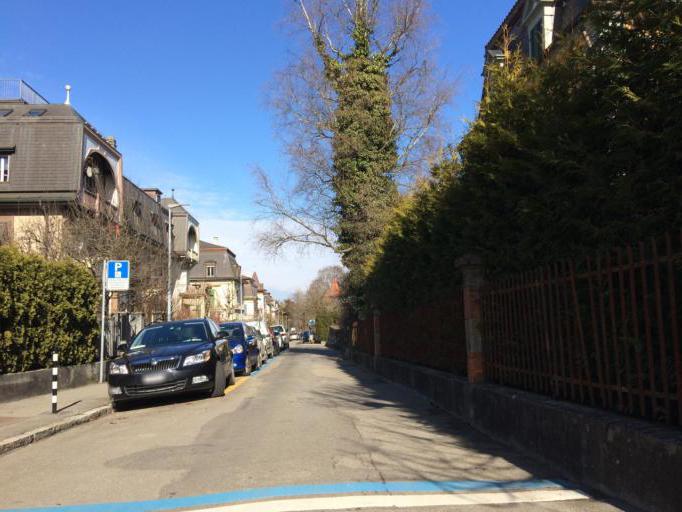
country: CH
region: Bern
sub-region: Bern-Mittelland District
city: Koniz
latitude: 46.9377
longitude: 7.4297
